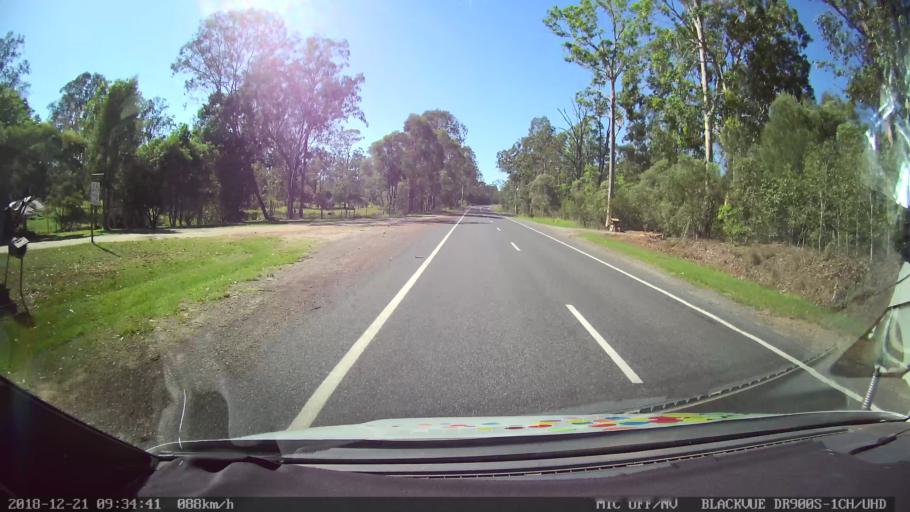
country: AU
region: New South Wales
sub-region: Clarence Valley
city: Grafton
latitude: -29.5010
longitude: 152.9811
